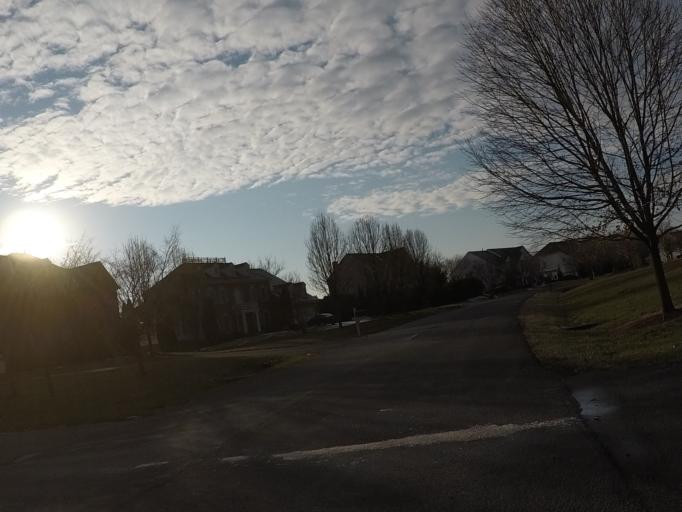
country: US
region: Maryland
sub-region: Howard County
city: Columbia
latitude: 39.2821
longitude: -76.9013
